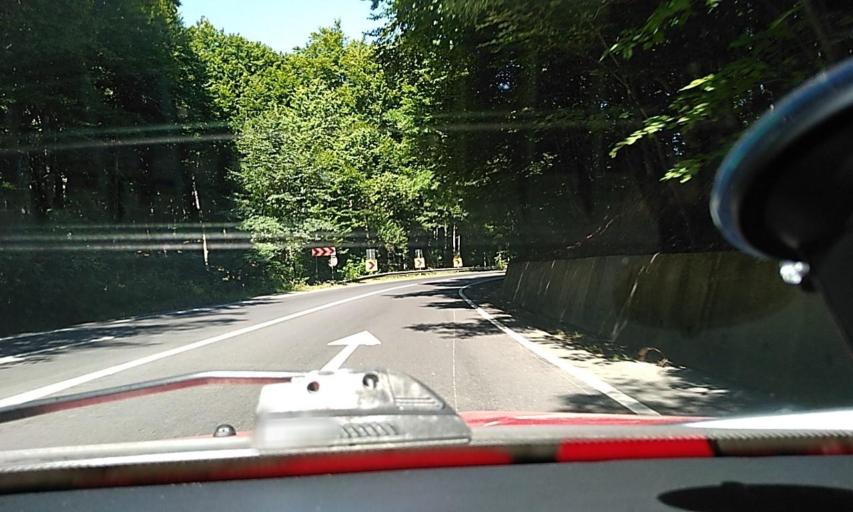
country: RO
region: Brasov
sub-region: Comuna Crizbav
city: Crizbav
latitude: 45.9010
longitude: 25.4366
